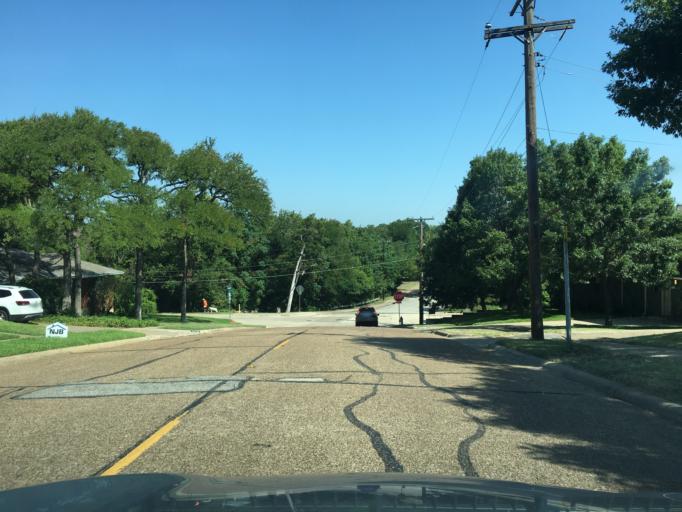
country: US
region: Texas
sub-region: Dallas County
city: Garland
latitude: 32.8539
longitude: -96.6924
